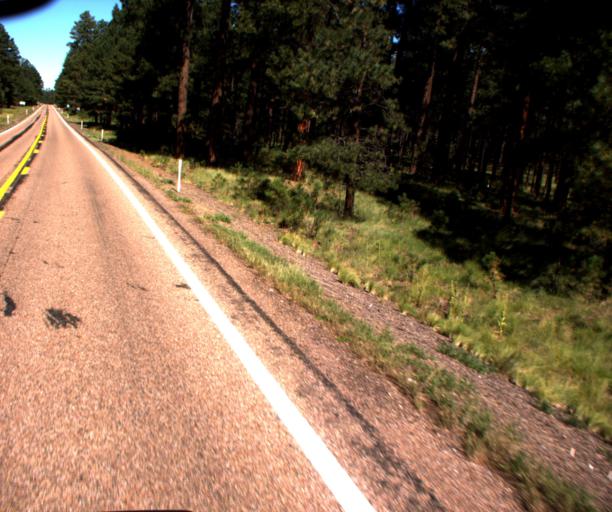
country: US
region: Arizona
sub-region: Navajo County
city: Pinetop-Lakeside
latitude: 34.0482
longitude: -109.7177
